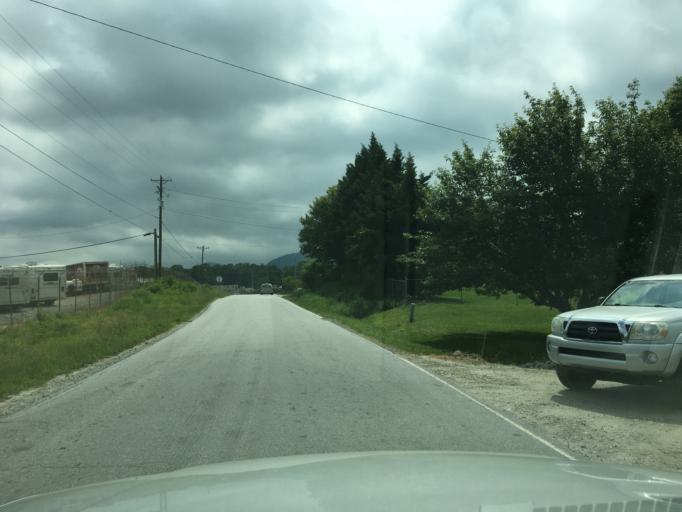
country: US
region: North Carolina
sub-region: Henderson County
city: Fletcher
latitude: 35.4133
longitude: -82.5079
